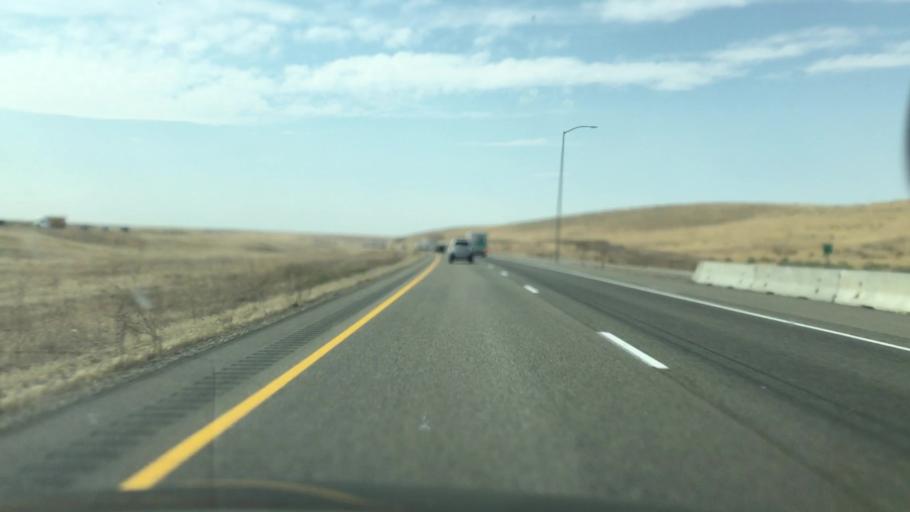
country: US
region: Idaho
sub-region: Ada County
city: Boise
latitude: 43.4802
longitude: -116.1080
